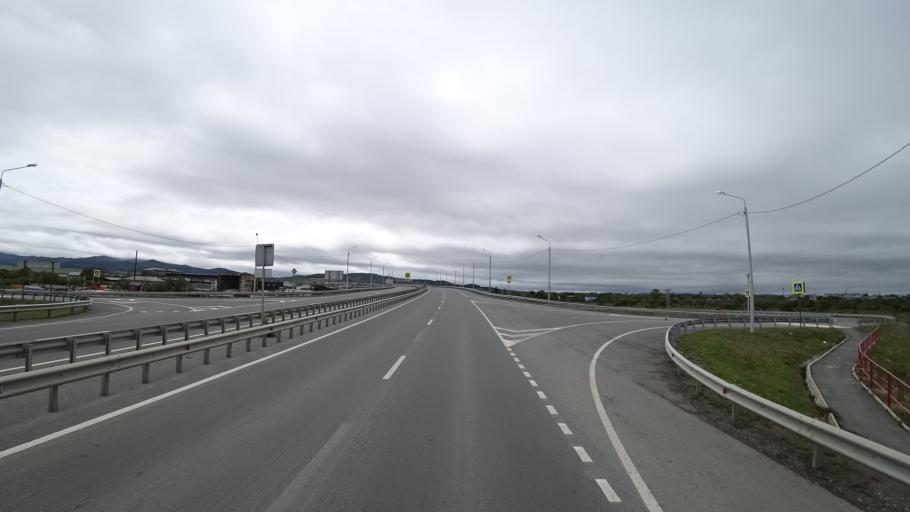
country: RU
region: Primorskiy
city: Monastyrishche
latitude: 44.1954
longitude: 132.4442
